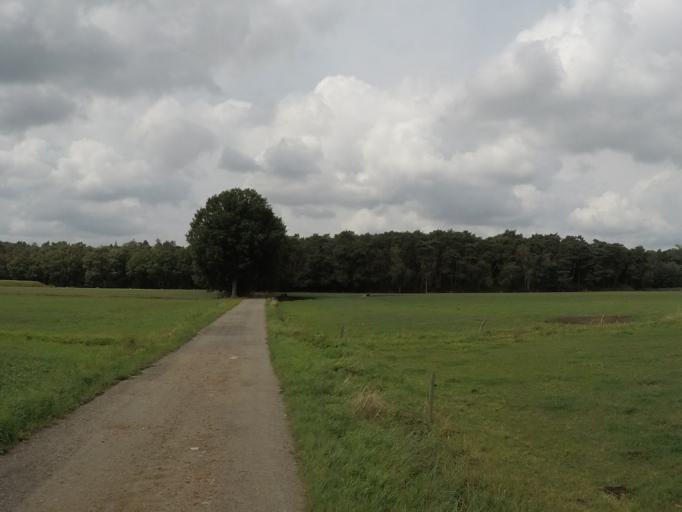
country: BE
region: Flanders
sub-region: Provincie Antwerpen
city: Grobbendonk
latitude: 51.2130
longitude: 4.7333
